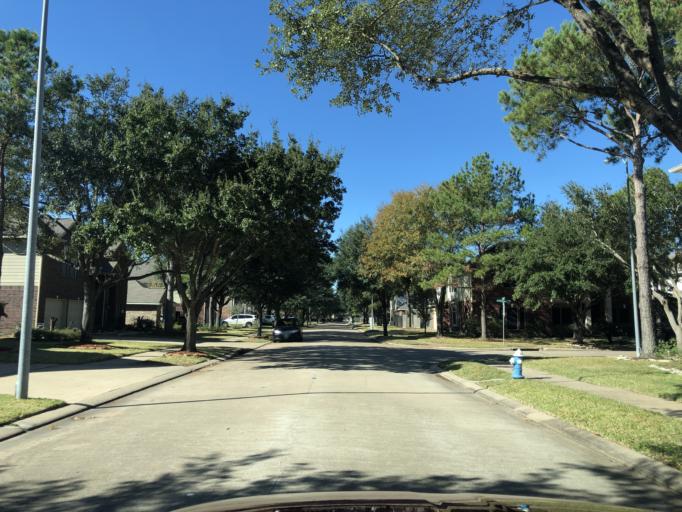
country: US
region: Texas
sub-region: Harris County
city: Oak Cliff Place
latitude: 29.9342
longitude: -95.6608
